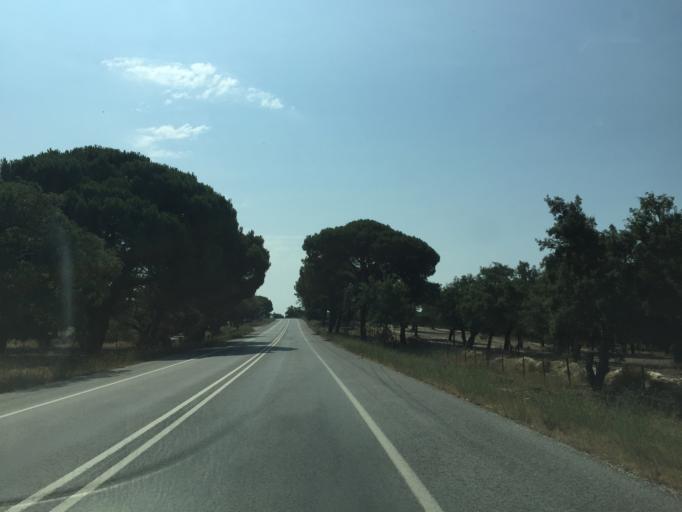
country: PT
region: Evora
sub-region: Vendas Novas
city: Vendas Novas
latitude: 38.5596
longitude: -8.6553
